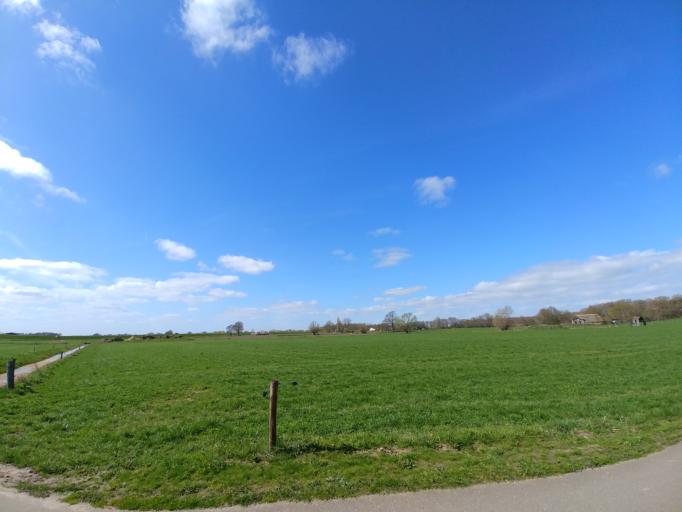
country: NL
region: Overijssel
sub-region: Gemeente Olst-Wijhe
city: Boskamp
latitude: 52.2954
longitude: 6.1217
